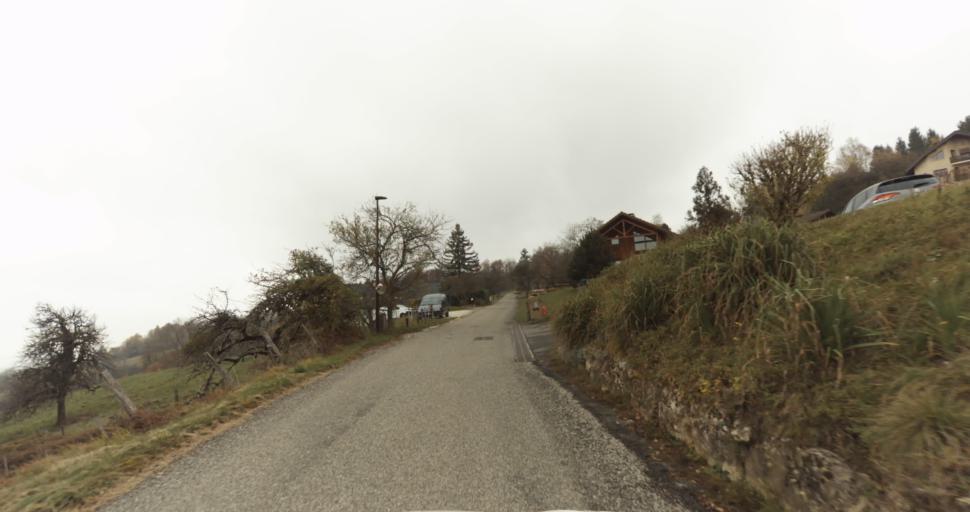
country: FR
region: Rhone-Alpes
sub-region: Departement de la Haute-Savoie
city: Viuz-la-Chiesaz
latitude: 45.8064
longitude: 6.0666
